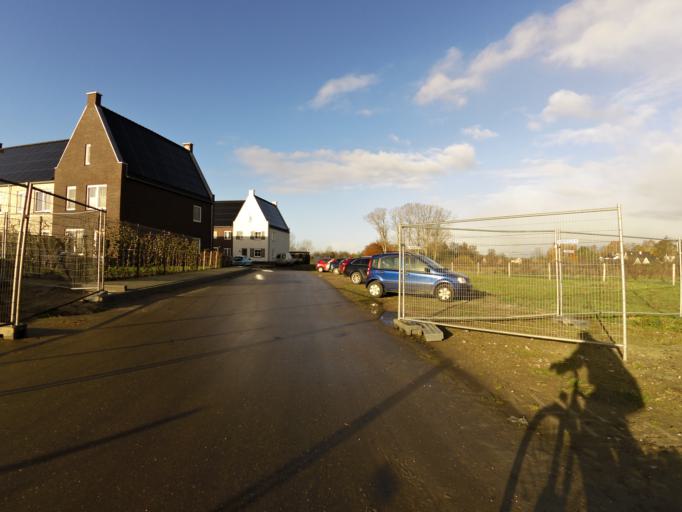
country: NL
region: Gelderland
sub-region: Gemeente Doetinchem
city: Doetinchem
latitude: 51.9547
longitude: 6.2795
